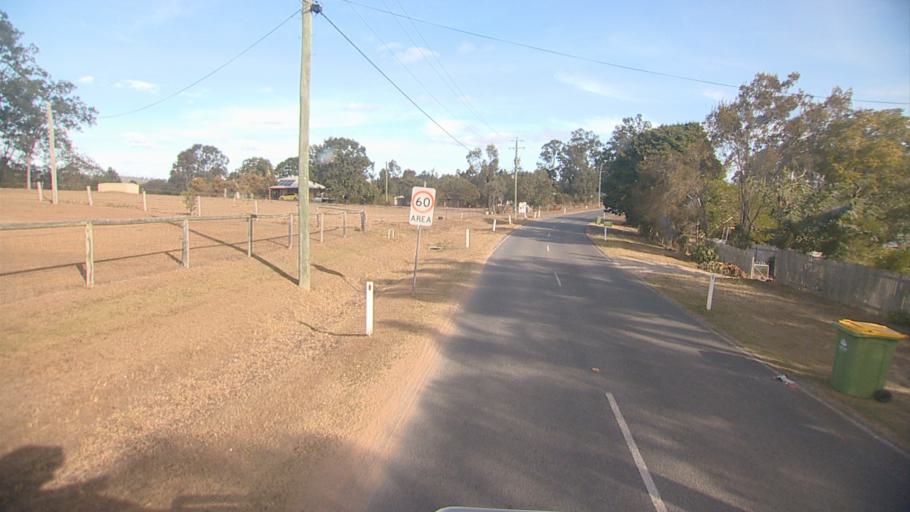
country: AU
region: Queensland
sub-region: Logan
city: Cedar Vale
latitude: -27.8655
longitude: 153.0057
